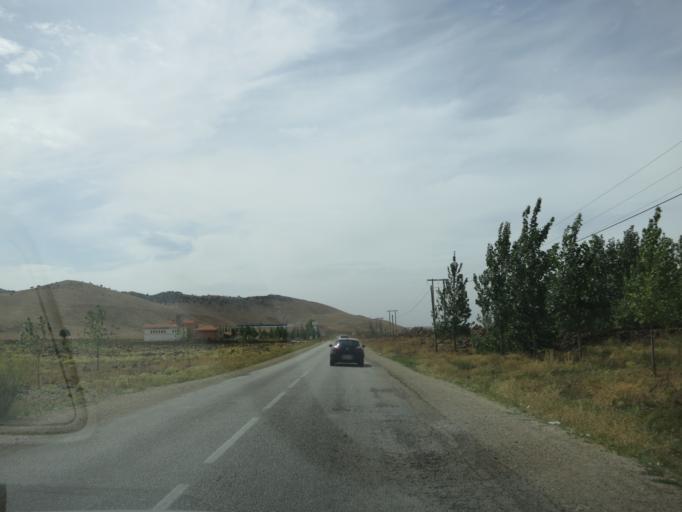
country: MA
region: Meknes-Tafilalet
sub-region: Ifrane
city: Azrou
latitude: 33.2239
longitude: -5.0600
